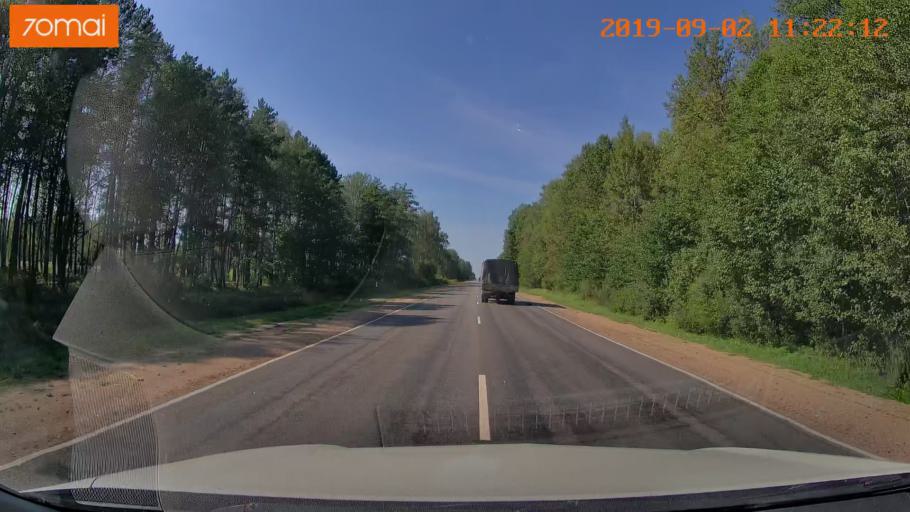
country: RU
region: Smolensk
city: Roslavl'
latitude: 54.0282
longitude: 33.0192
